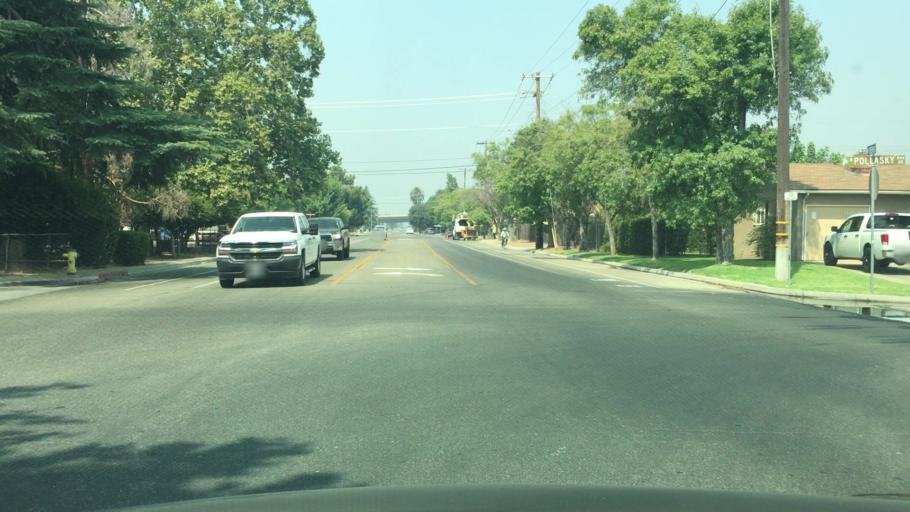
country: US
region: California
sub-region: Fresno County
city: Clovis
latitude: 36.8304
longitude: -119.7020
